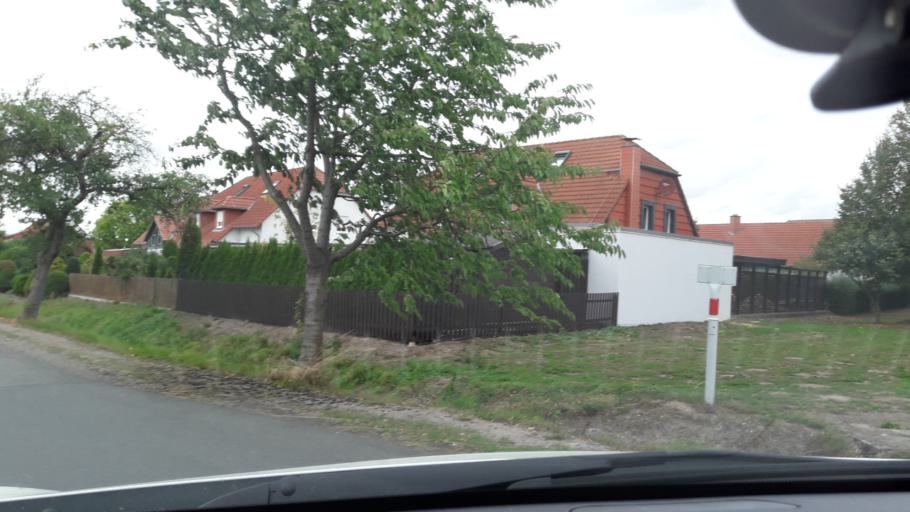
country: DE
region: Lower Saxony
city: Flothe
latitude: 52.0842
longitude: 10.4735
